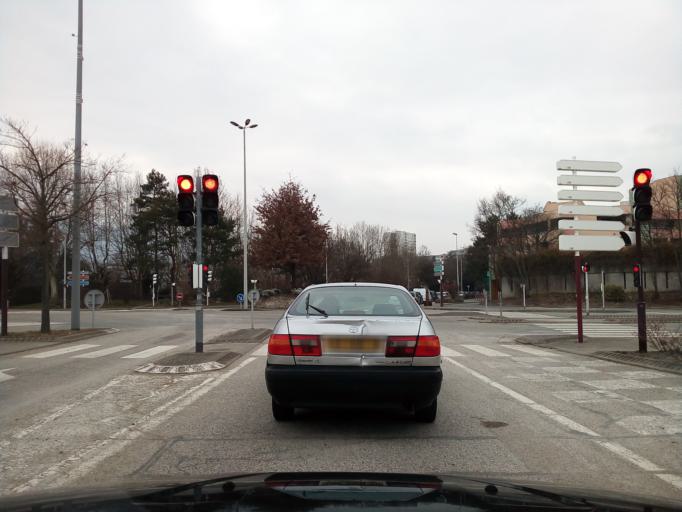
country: FR
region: Rhone-Alpes
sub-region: Departement de l'Isere
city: Echirolles
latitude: 45.1530
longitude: 5.7240
